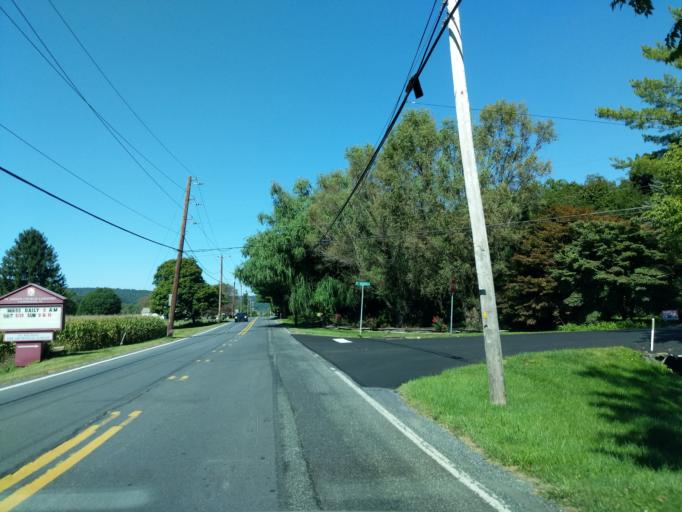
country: US
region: Pennsylvania
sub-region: Lehigh County
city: Emmaus
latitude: 40.5146
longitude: -75.4486
